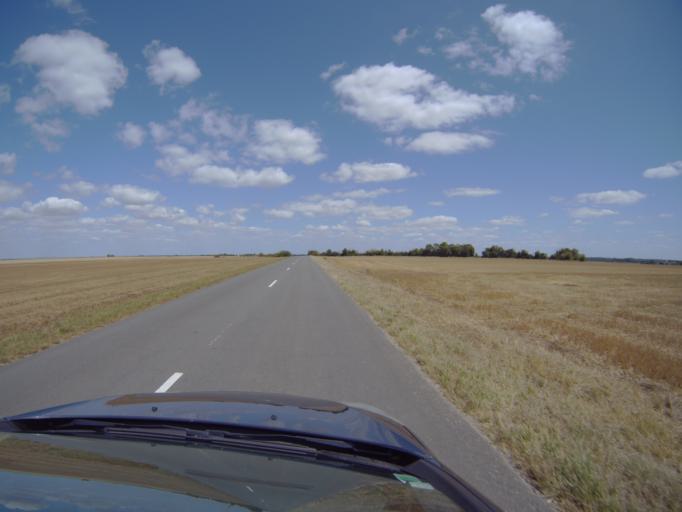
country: FR
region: Poitou-Charentes
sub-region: Departement des Deux-Sevres
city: Saint-Hilaire-la-Palud
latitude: 46.2652
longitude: -0.6784
